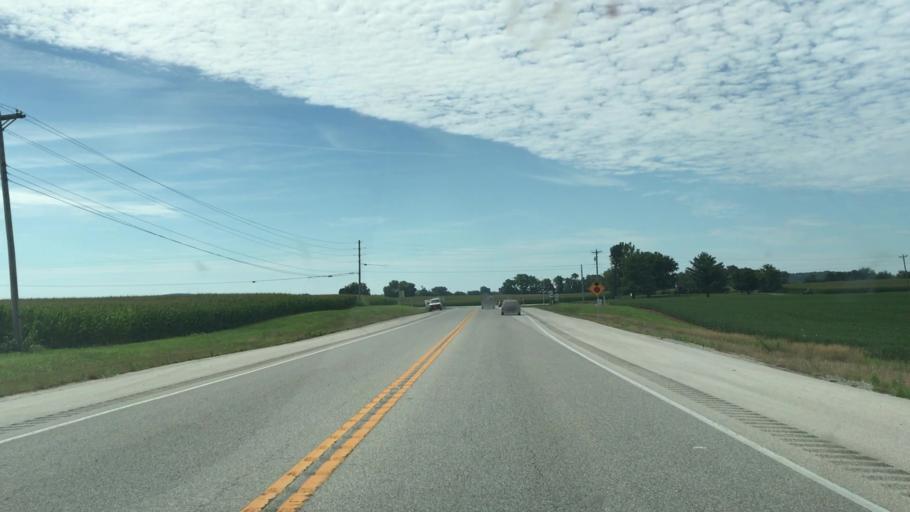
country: US
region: Kentucky
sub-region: Edmonson County
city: Brownsville
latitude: 37.0877
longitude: -86.2299
